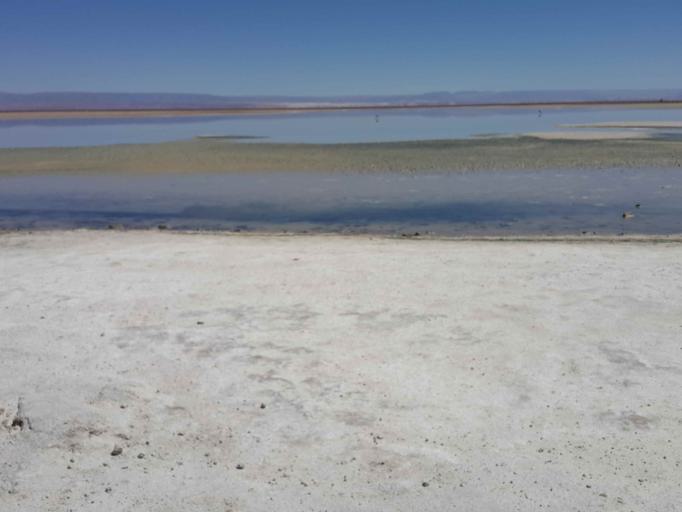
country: CL
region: Antofagasta
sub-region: Provincia de El Loa
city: San Pedro de Atacama
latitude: -23.2885
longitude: -68.1766
